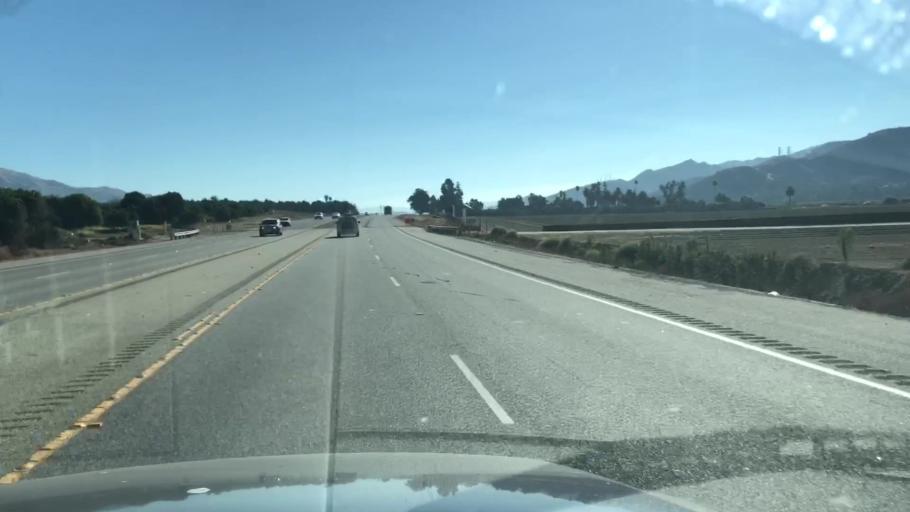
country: US
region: California
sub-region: Ventura County
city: Piru
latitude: 34.4074
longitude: -118.7649
